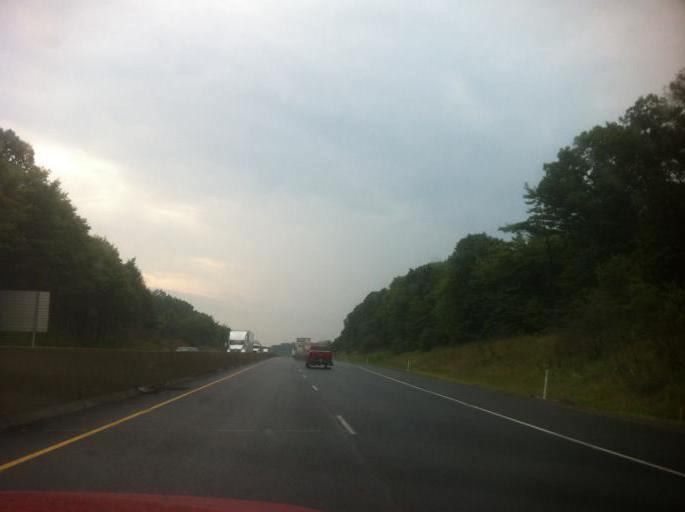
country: US
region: Pennsylvania
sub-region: Clarion County
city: Clarion
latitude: 41.1899
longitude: -79.4184
